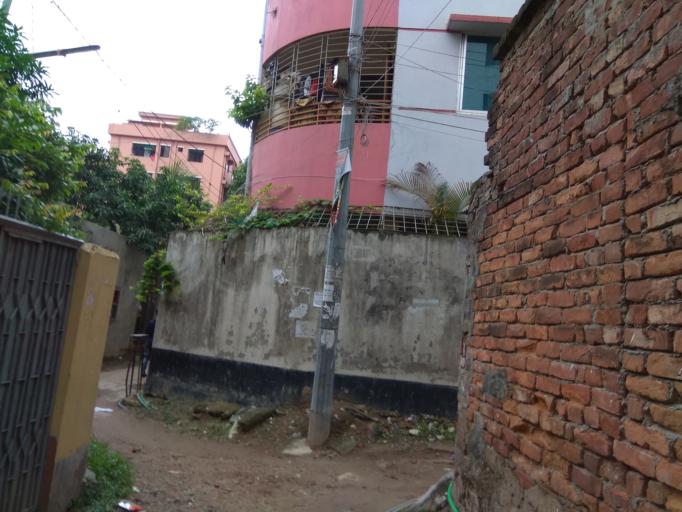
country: BD
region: Dhaka
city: Azimpur
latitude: 23.7934
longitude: 90.3711
